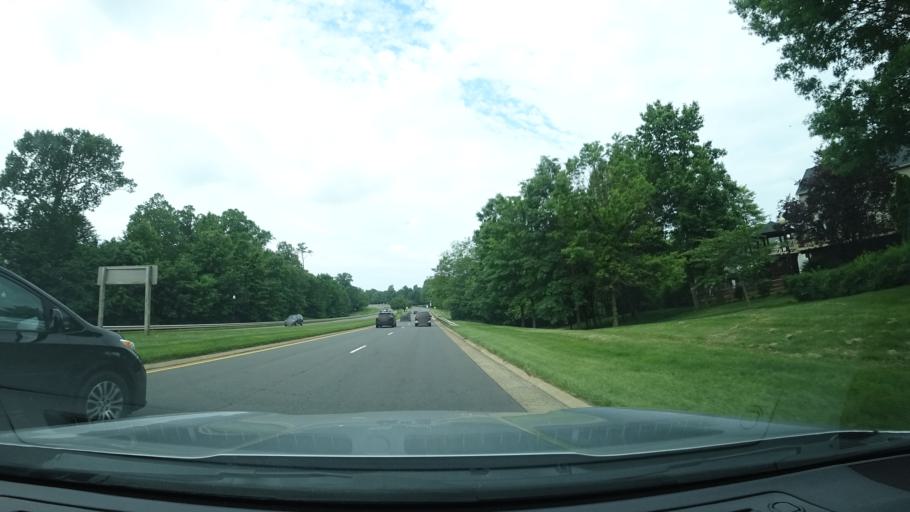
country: US
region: Virginia
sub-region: Loudoun County
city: Sugarland Run
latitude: 39.0441
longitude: -77.3921
